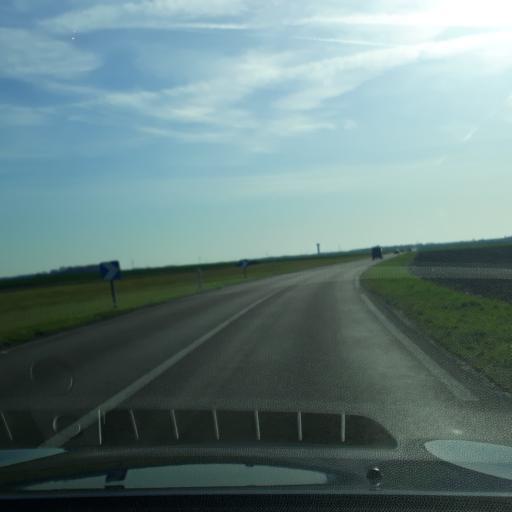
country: FR
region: Ile-de-France
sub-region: Departement de l'Essonne
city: Corbreuse
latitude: 48.4500
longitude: 1.9651
